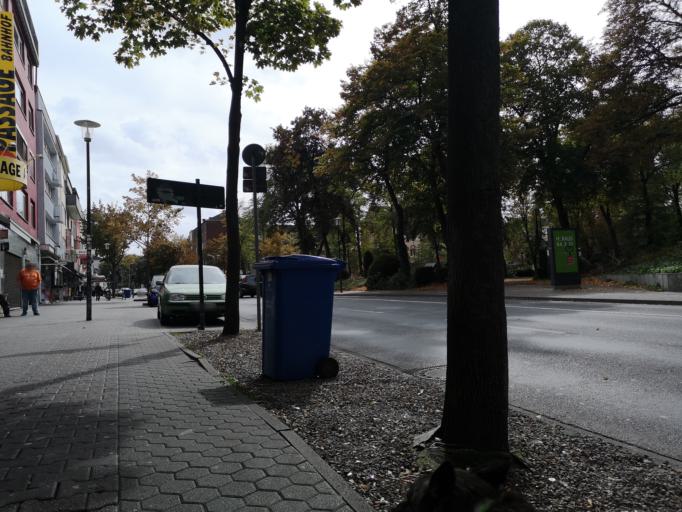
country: DE
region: North Rhine-Westphalia
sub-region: Regierungsbezirk Koln
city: Dueren
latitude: 50.8078
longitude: 6.4808
